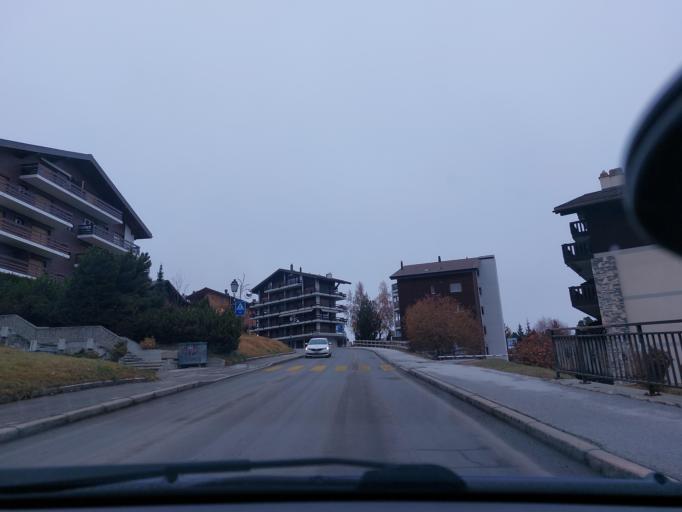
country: CH
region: Valais
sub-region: Conthey District
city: Basse-Nendaz
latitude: 46.1807
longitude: 7.2940
